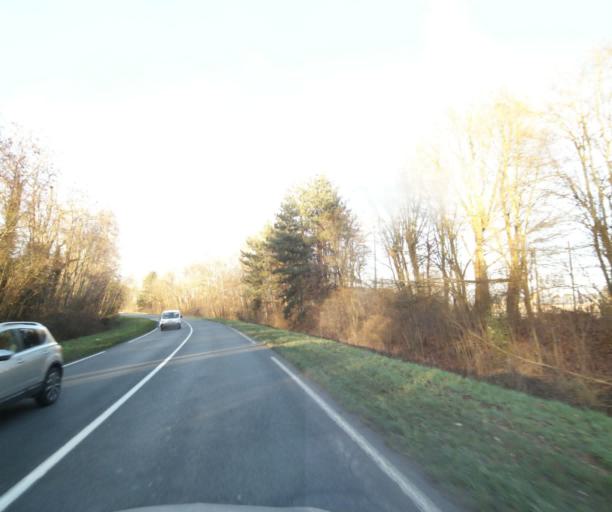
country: FR
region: Nord-Pas-de-Calais
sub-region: Departement du Nord
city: Famars
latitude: 50.3264
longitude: 3.5179
